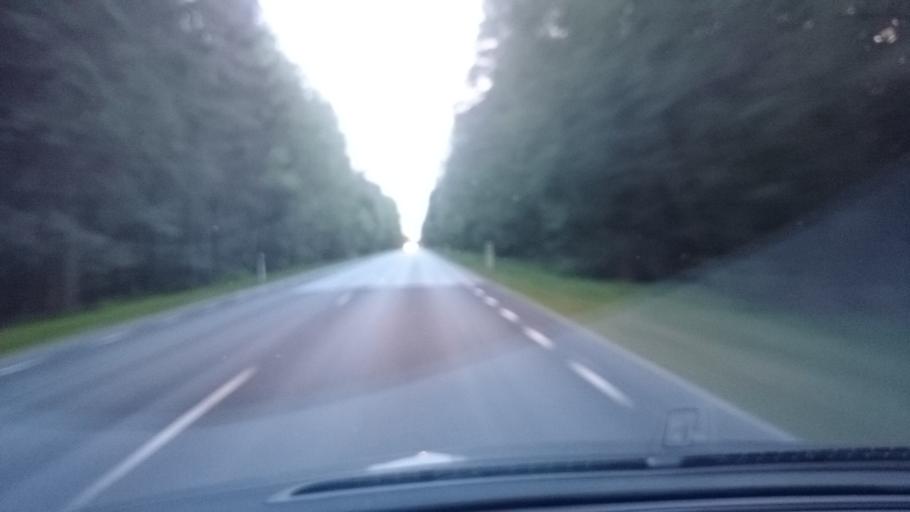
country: EE
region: Raplamaa
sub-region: Kehtna vald
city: Kehtna
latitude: 58.8456
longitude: 25.0458
